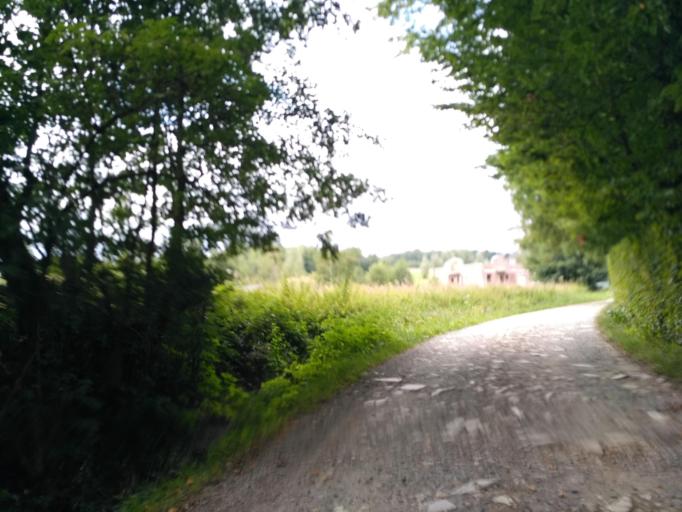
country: PL
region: Subcarpathian Voivodeship
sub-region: Powiat rzeszowski
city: Tyczyn
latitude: 49.9374
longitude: 22.0792
